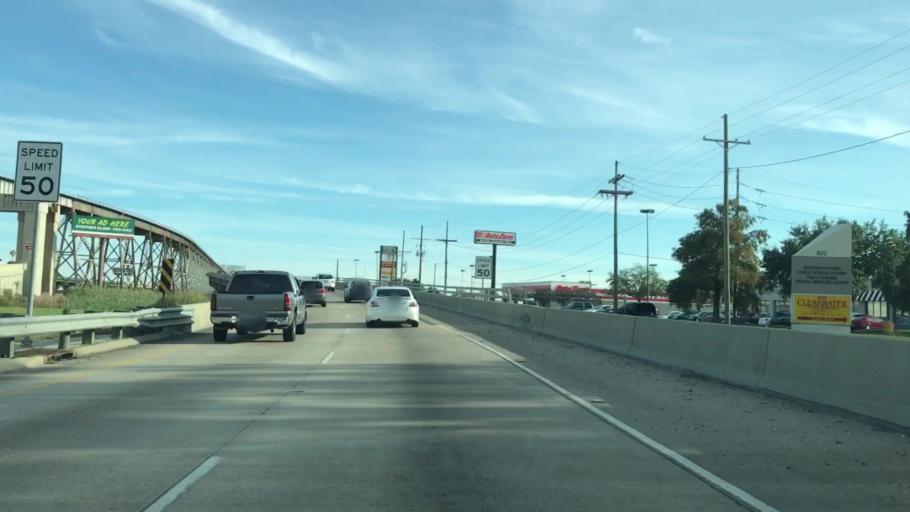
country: US
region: Louisiana
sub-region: Jefferson Parish
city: Elmwood
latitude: 29.9551
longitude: -90.1819
